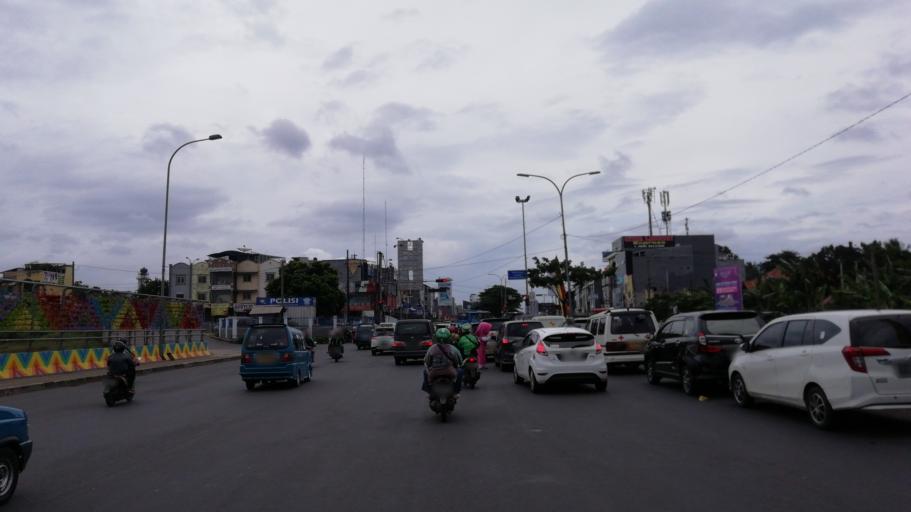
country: ID
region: West Java
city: Depok
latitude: -6.3760
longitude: 106.8322
